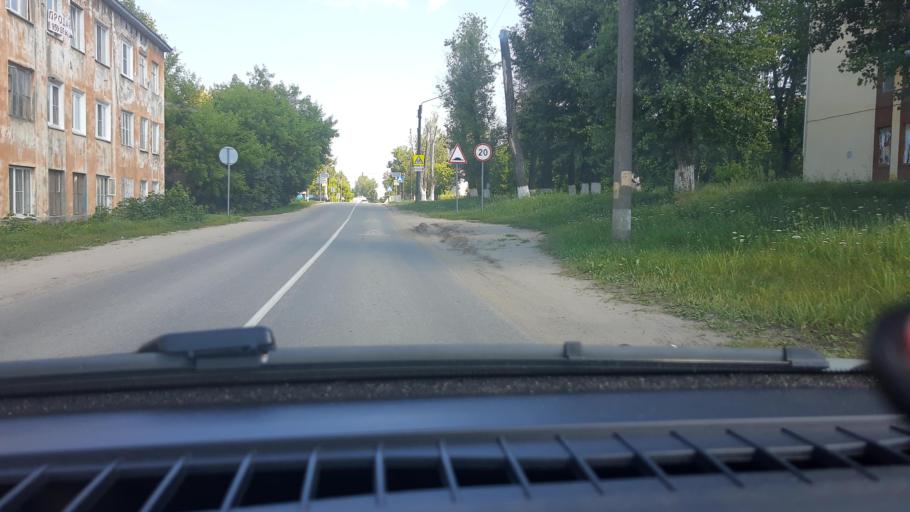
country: RU
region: Nizjnij Novgorod
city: Afonino
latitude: 56.2847
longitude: 44.1907
